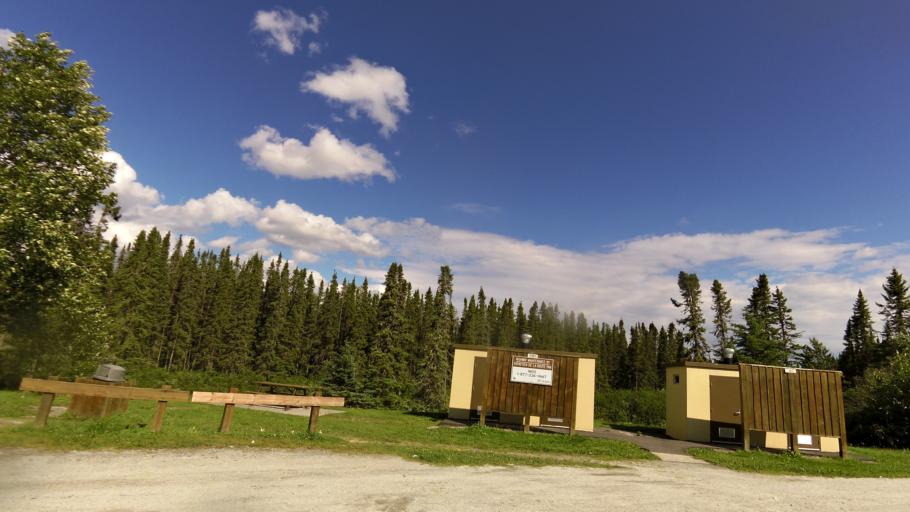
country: CA
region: Ontario
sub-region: Algoma
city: Hornepayne
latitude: 49.7675
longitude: -84.7718
